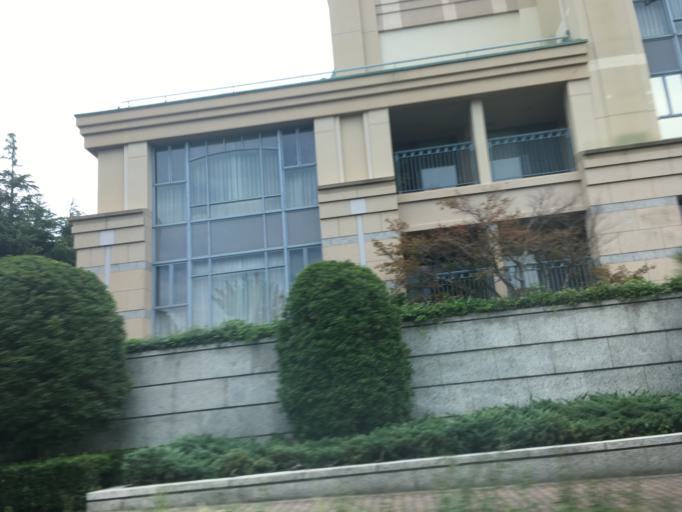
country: JP
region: Hyogo
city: Ashiya
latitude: 34.7231
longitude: 135.2645
